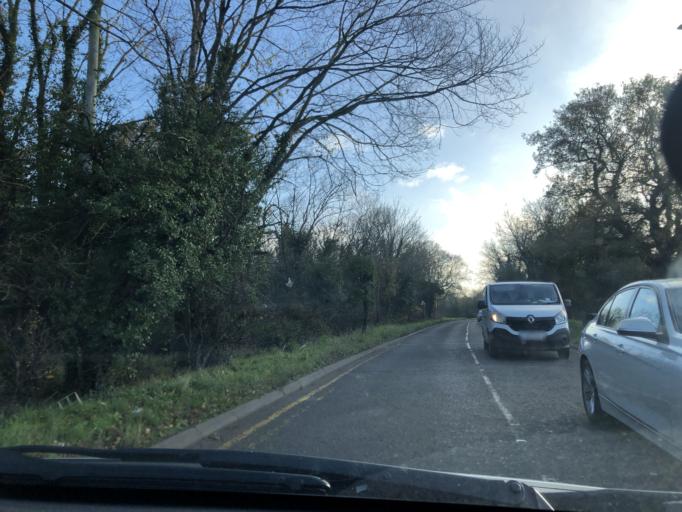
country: GB
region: England
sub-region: Greater London
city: Bexley
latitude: 51.4422
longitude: 0.1811
